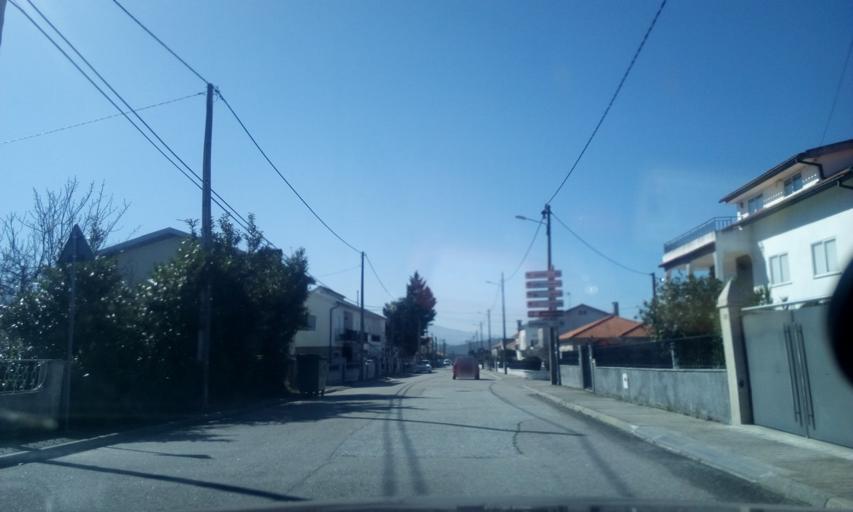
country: PT
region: Guarda
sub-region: Celorico da Beira
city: Celorico da Beira
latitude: 40.6232
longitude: -7.4047
